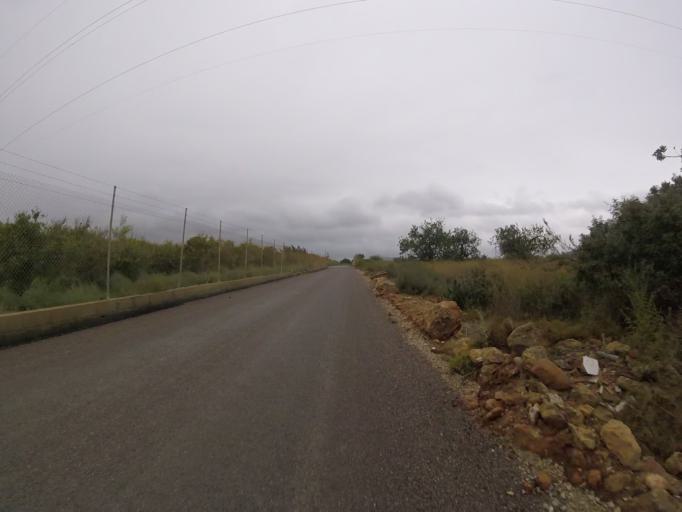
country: ES
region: Valencia
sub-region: Provincia de Castello
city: Alcoceber
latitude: 40.2380
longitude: 0.2512
